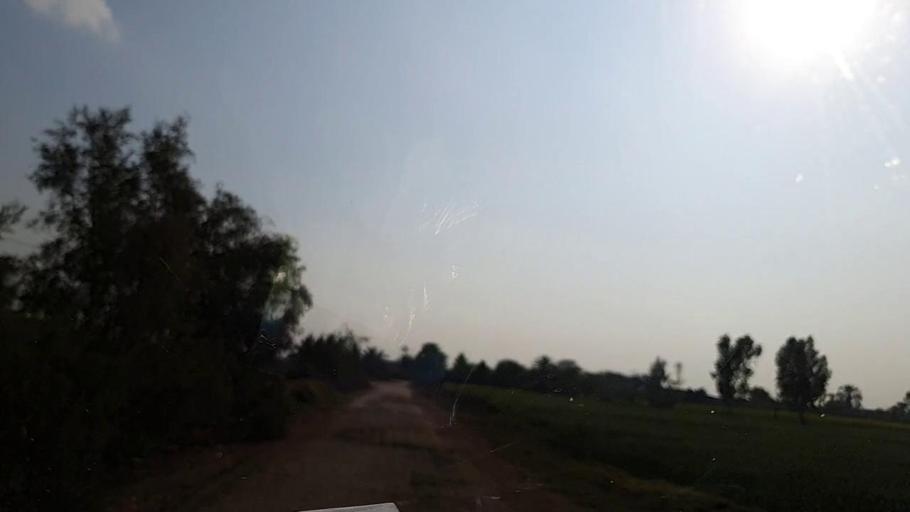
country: PK
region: Sindh
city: Nawabshah
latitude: 26.1459
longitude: 68.3900
